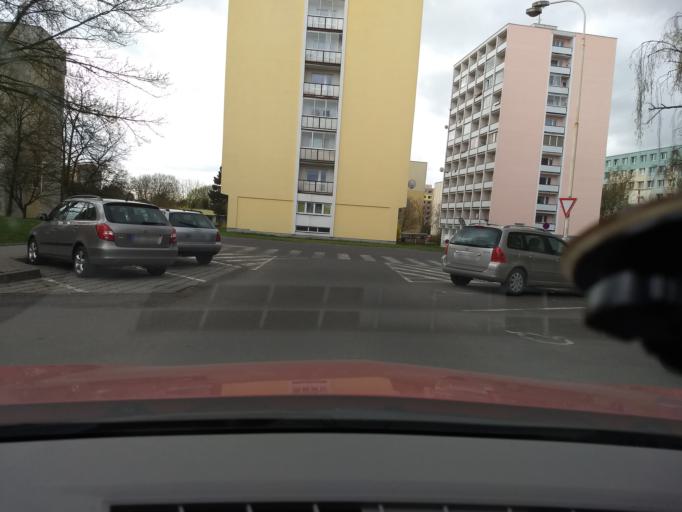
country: CZ
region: Central Bohemia
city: Kladno
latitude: 50.1316
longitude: 14.1224
